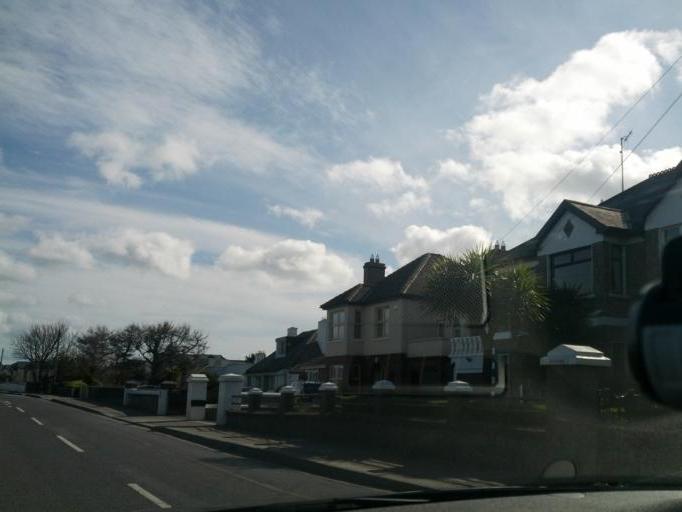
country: IE
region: Leinster
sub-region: Fingal County
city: Baldoyle
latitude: 53.3961
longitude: -6.1249
